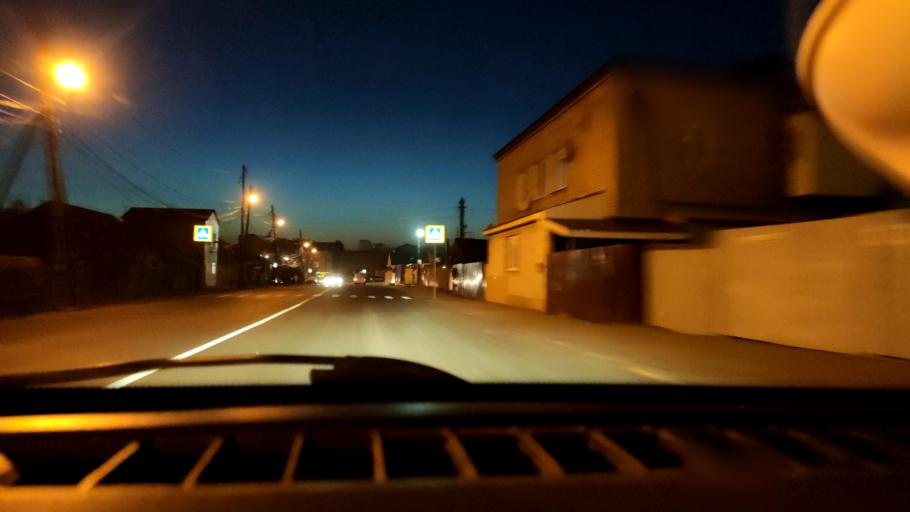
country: RU
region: Samara
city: Samara
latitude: 53.1831
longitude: 50.1278
